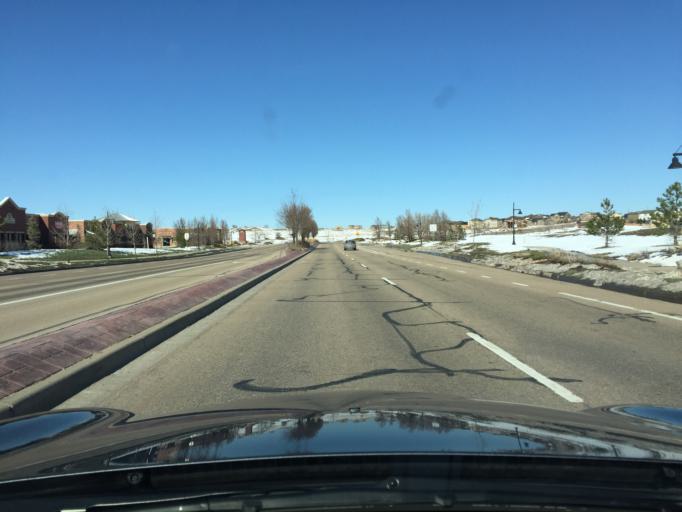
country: US
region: Colorado
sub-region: Boulder County
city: Erie
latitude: 40.0412
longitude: -105.0464
